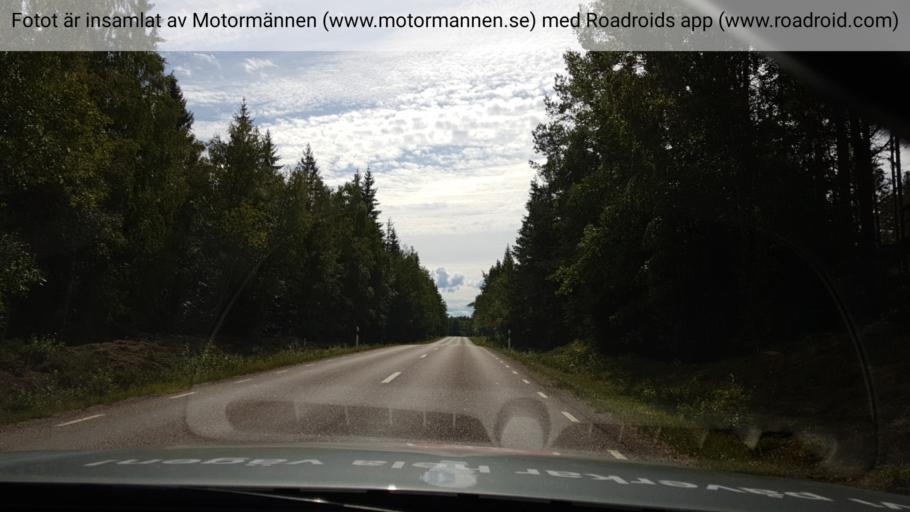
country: SE
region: Uppsala
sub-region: Heby Kommun
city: OEstervala
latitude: 60.0047
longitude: 17.3009
